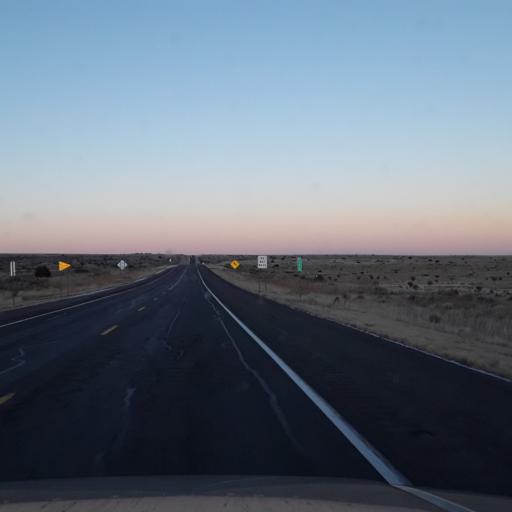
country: US
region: New Mexico
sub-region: Guadalupe County
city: Santa Rosa
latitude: 34.5371
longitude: -105.3132
